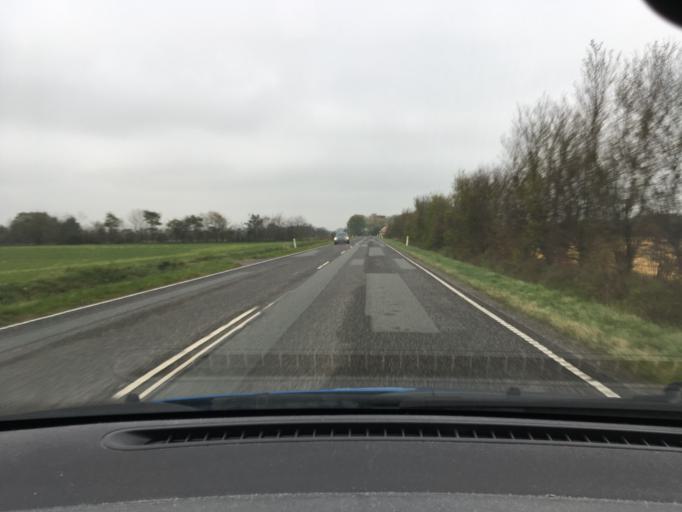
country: DK
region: South Denmark
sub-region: Aabenraa Kommune
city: Rodekro
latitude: 55.0708
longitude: 9.1858
